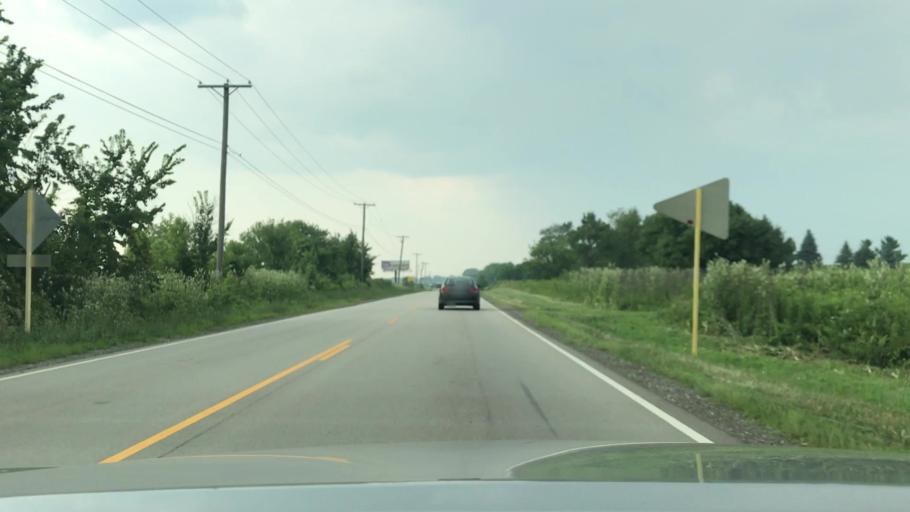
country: US
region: Illinois
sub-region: Will County
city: Plainfield
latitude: 41.6760
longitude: -88.2475
